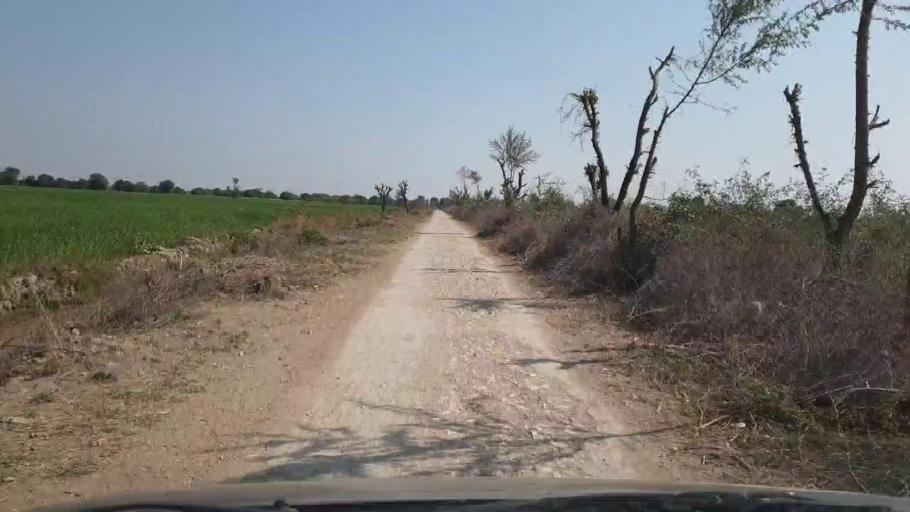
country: PK
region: Sindh
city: Digri
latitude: 25.2037
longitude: 69.2327
